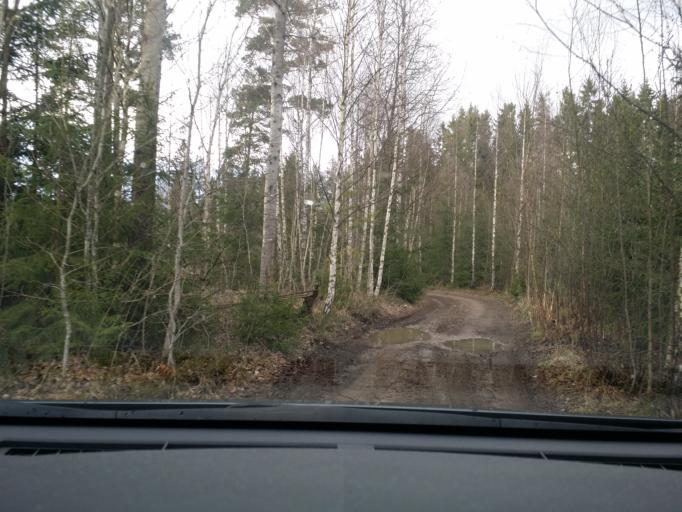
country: SE
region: Soedermanland
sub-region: Eskilstuna Kommun
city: Arla
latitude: 59.3737
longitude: 16.6538
